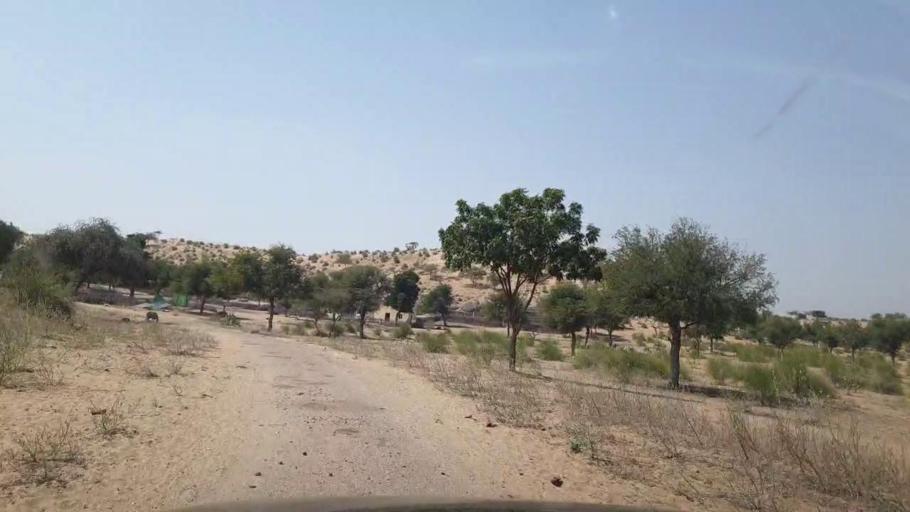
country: PK
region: Sindh
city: Islamkot
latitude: 25.1190
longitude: 70.7530
